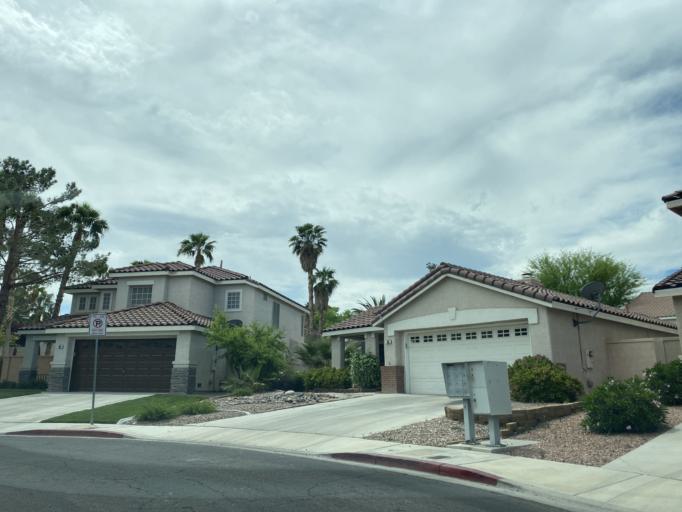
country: US
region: Nevada
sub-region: Clark County
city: Whitney
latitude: 36.0244
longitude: -115.0709
